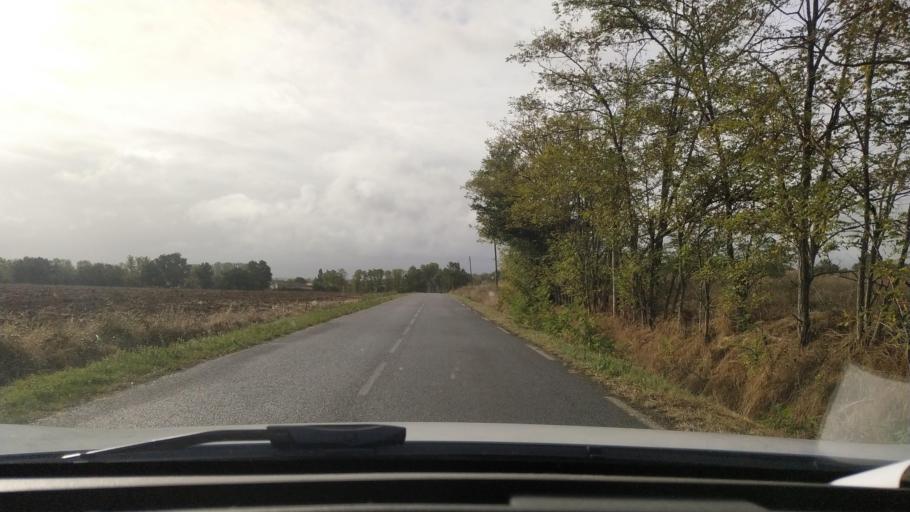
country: FR
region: Midi-Pyrenees
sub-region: Departement de la Haute-Garonne
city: Auterive
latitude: 43.3058
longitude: 1.4659
